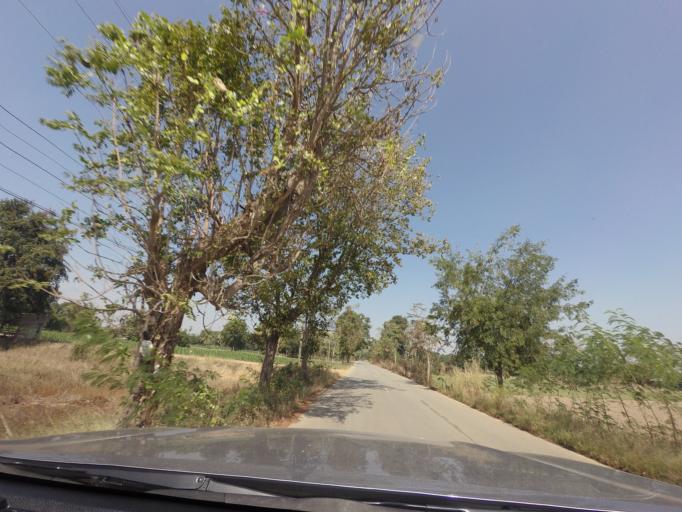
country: TH
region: Sukhothai
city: Si Samrong
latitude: 17.2080
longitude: 99.7750
